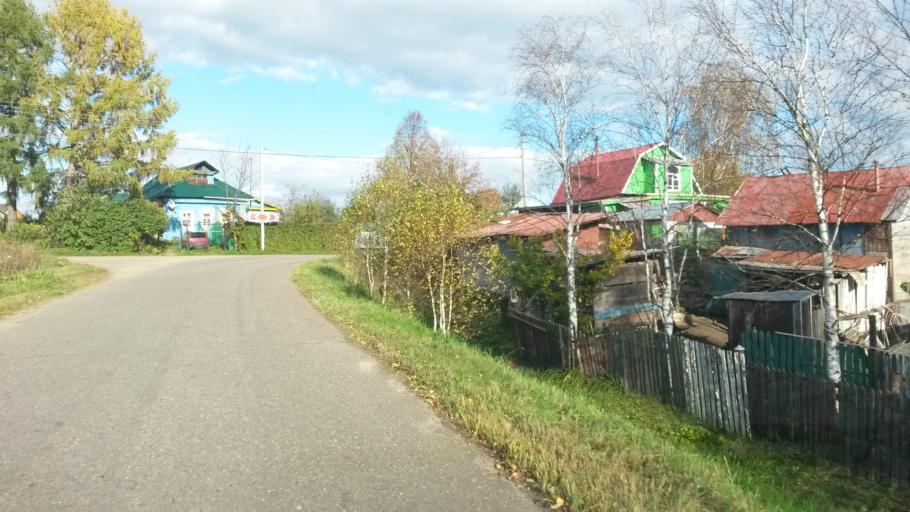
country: RU
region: Jaroslavl
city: Tunoshna
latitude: 57.5263
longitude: 39.9797
